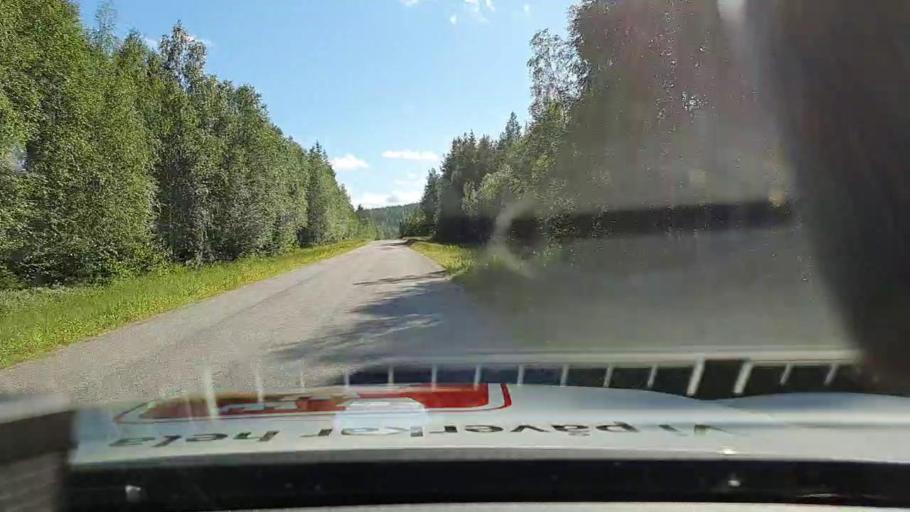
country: SE
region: Norrbotten
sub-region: Overkalix Kommun
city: OEverkalix
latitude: 66.2505
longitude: 23.0111
